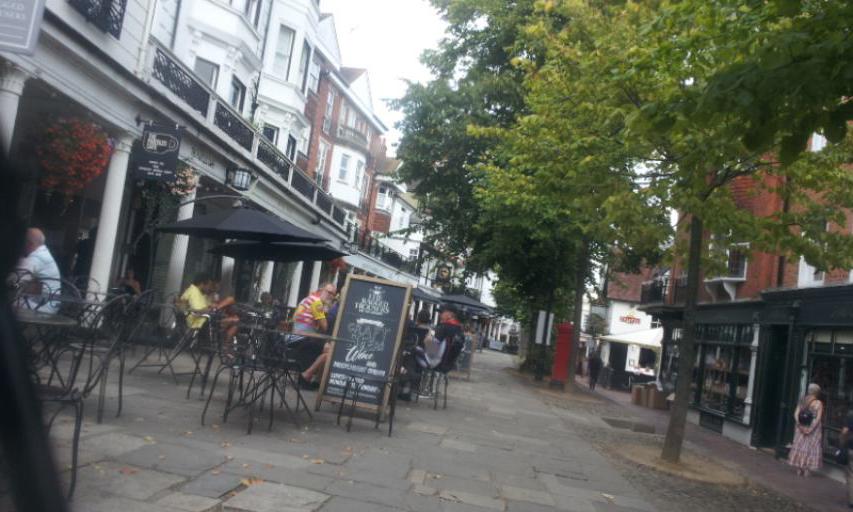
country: GB
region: England
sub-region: Kent
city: Royal Tunbridge Wells
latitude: 51.1259
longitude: 0.2577
